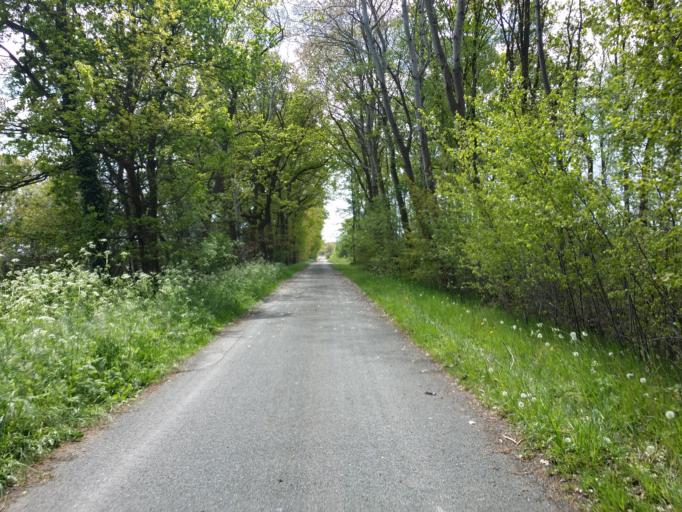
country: DE
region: Lower Saxony
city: Gross Ippener
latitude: 52.9801
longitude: 8.6048
